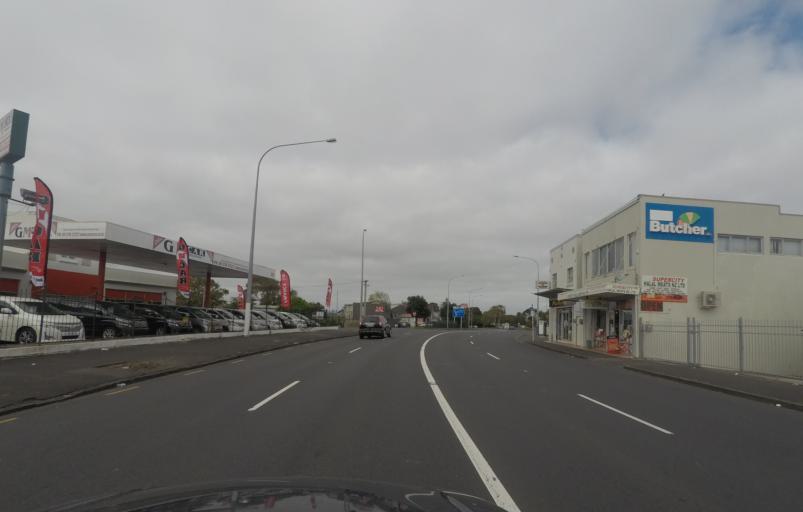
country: NZ
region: Auckland
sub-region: Auckland
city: Mangere
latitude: -36.9481
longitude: 174.8458
